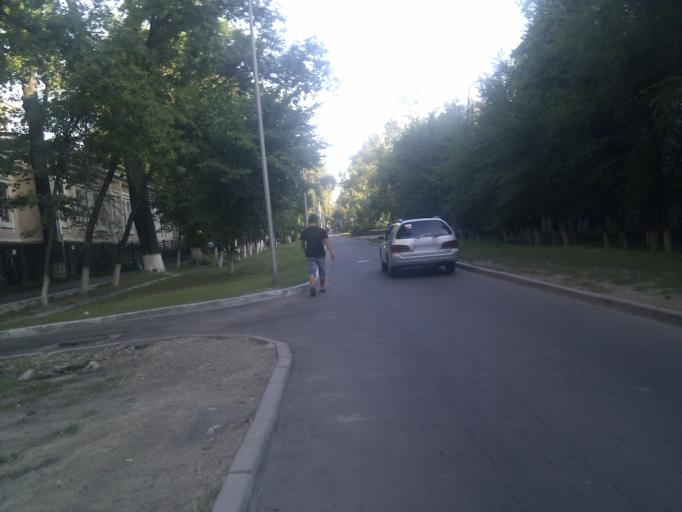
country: KZ
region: Almaty Qalasy
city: Almaty
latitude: 43.2566
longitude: 76.9518
